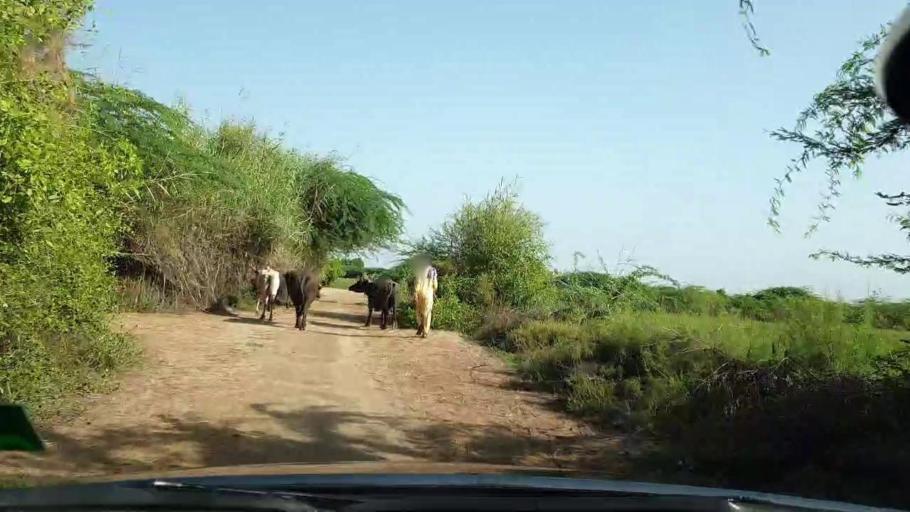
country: PK
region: Sindh
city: Tando Bago
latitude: 24.6634
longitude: 69.0428
